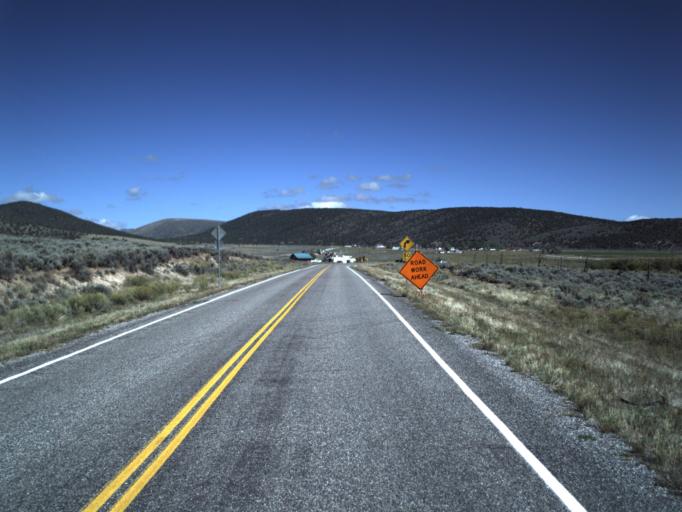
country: US
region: Utah
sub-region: Sevier County
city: Monroe
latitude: 38.5516
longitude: -111.8665
